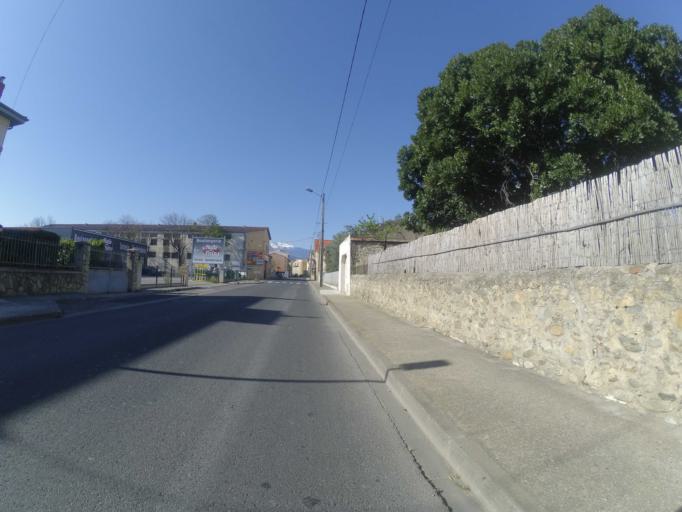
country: FR
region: Languedoc-Roussillon
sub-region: Departement des Pyrenees-Orientales
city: Ille-sur-Tet
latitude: 42.6735
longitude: 2.6242
